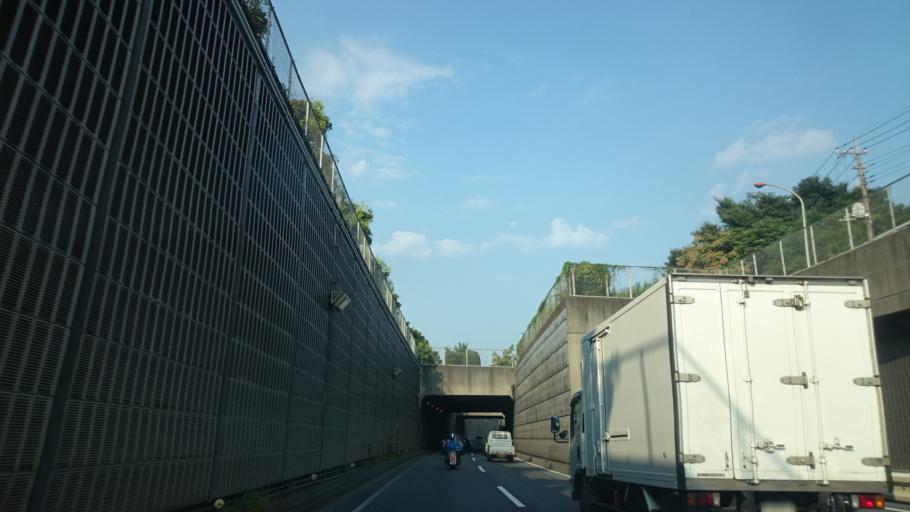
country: JP
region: Saitama
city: Ageoshimo
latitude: 35.9611
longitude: 139.6281
